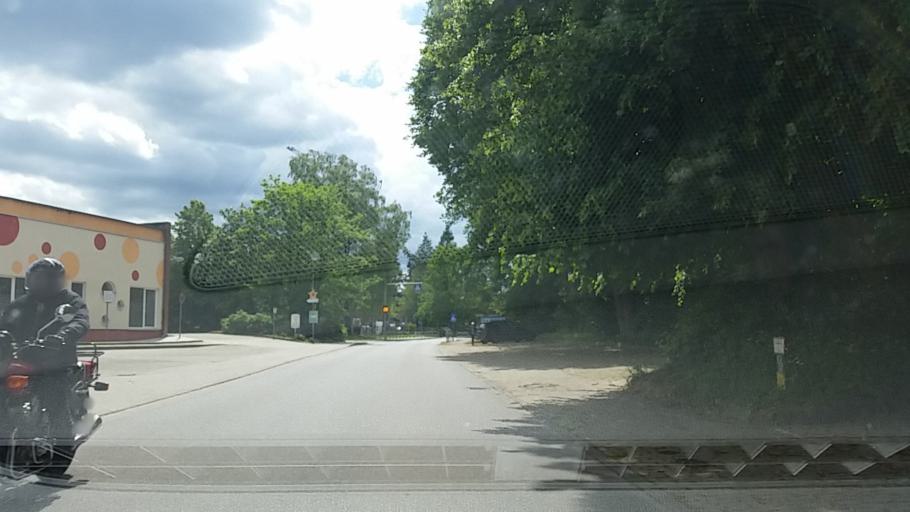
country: DE
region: Schleswig-Holstein
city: Kuddeworde
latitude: 53.5813
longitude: 10.3951
